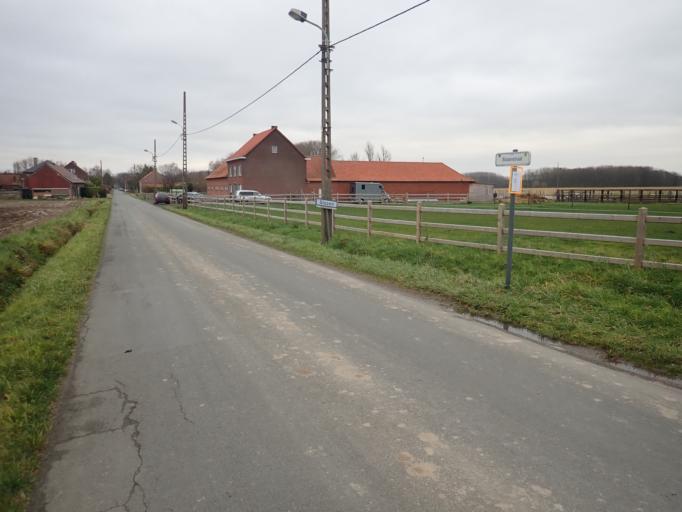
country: BE
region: Flanders
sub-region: Provincie Vlaams-Brabant
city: Londerzeel
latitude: 50.9800
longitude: 4.2899
